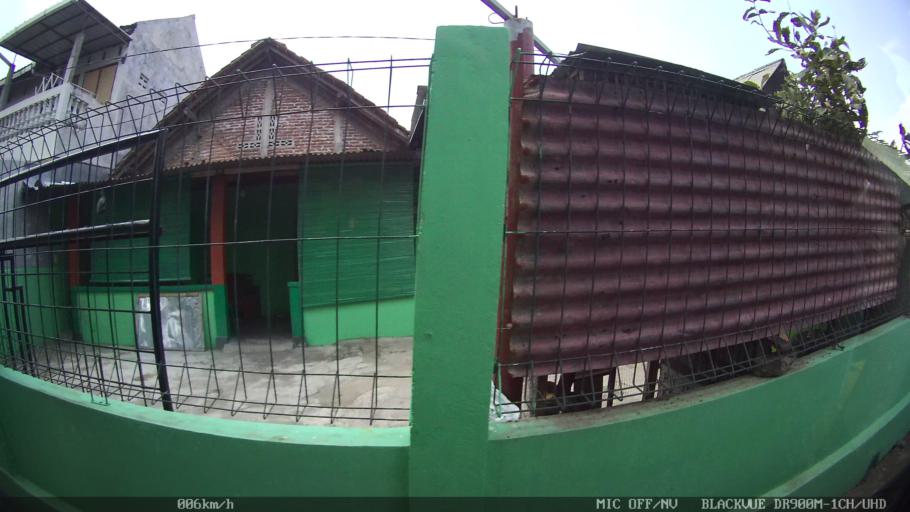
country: ID
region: Daerah Istimewa Yogyakarta
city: Yogyakarta
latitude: -7.8150
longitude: 110.3989
